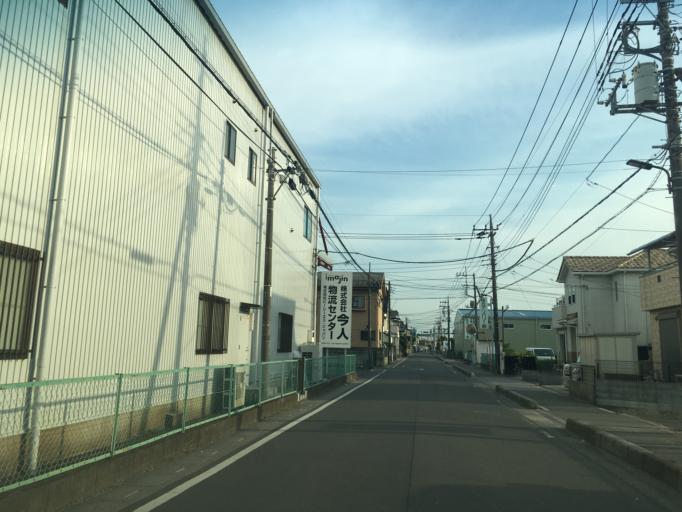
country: JP
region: Saitama
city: Koshigaya
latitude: 35.8595
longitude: 139.8113
